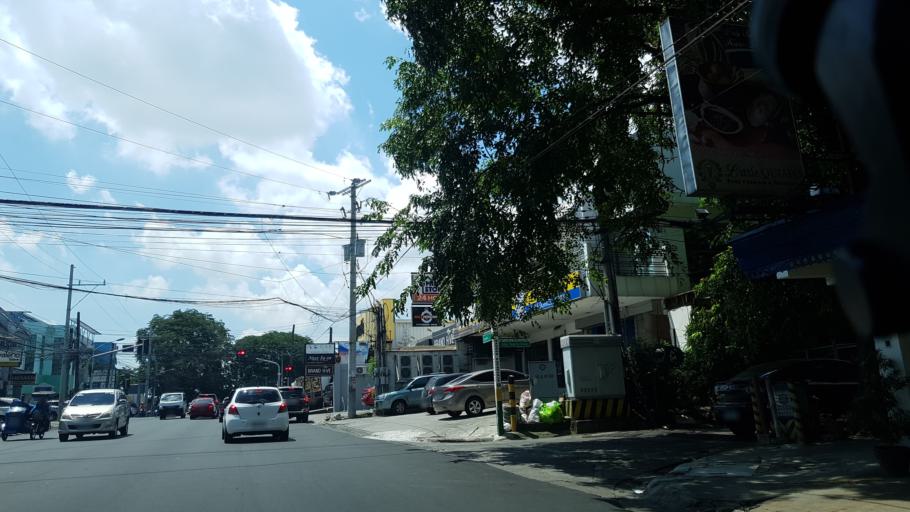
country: PH
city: Sambayanihan People's Village
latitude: 14.4450
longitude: 121.0258
